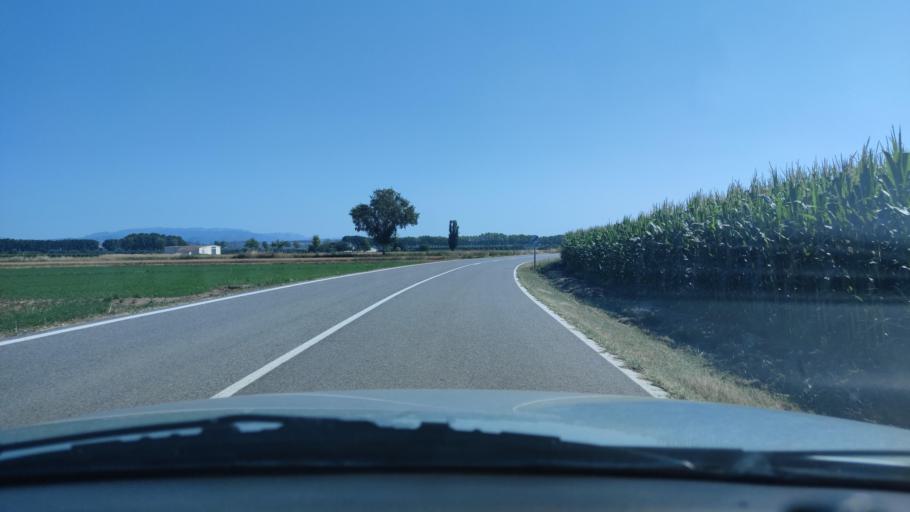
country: ES
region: Catalonia
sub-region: Provincia de Lleida
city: Linyola
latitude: 41.7210
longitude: 0.9168
